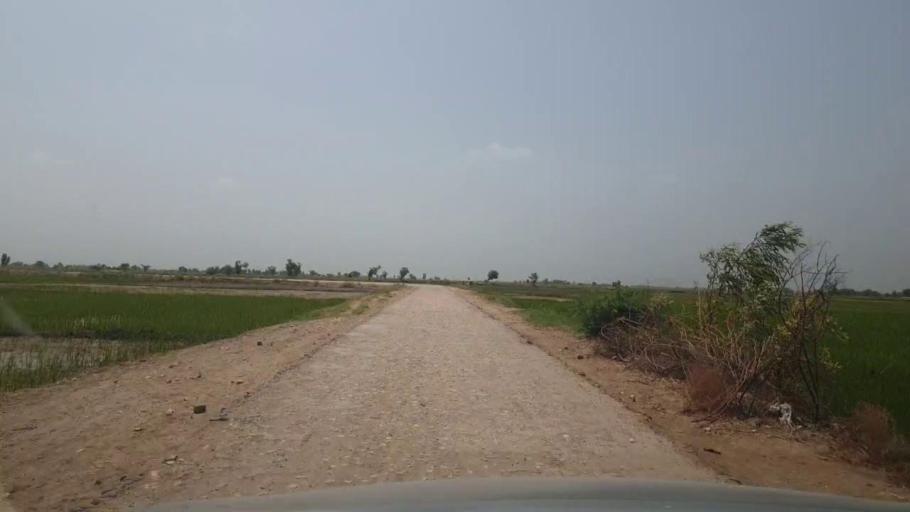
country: PK
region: Sindh
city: Garhi Yasin
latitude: 27.9379
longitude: 68.3895
